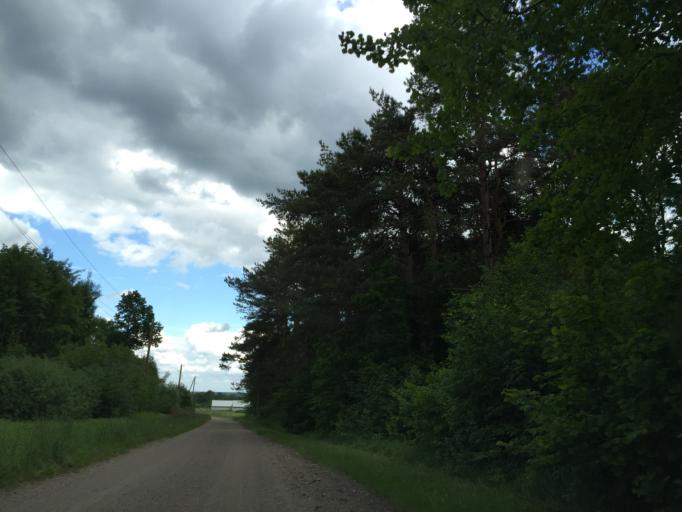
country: LV
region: Dobeles Rajons
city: Dobele
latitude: 56.6575
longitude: 23.2965
